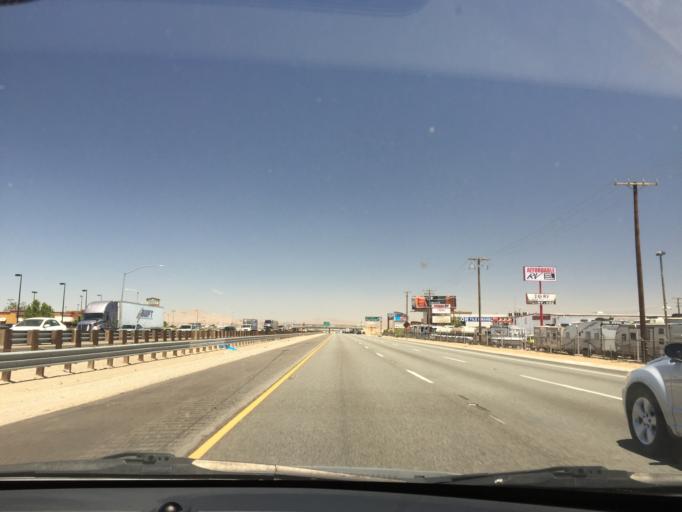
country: US
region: California
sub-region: San Bernardino County
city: Mountain View Acres
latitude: 34.4651
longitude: -117.3503
